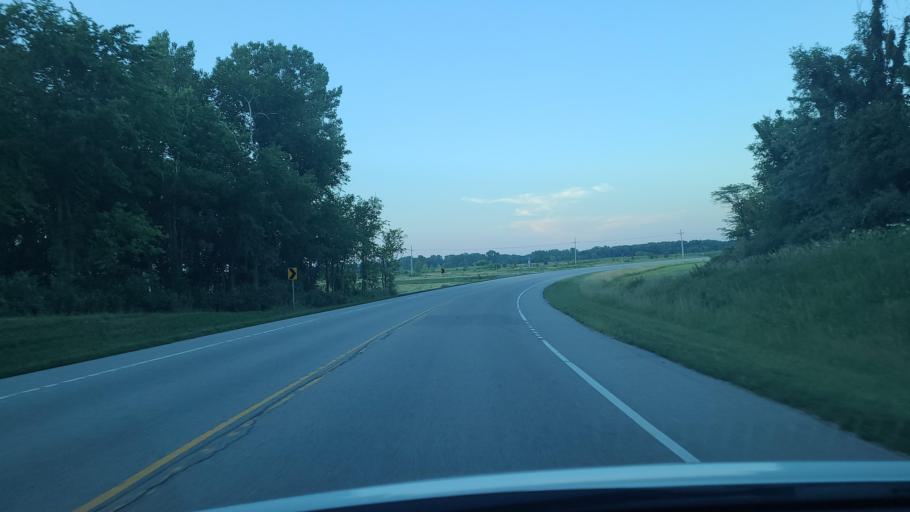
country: US
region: Kansas
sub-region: Douglas County
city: Lawrence
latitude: 38.9114
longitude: -95.3162
